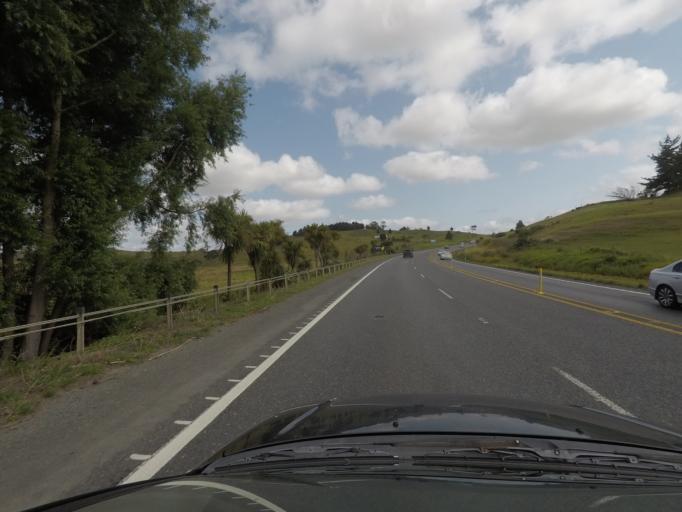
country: NZ
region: Northland
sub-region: Whangarei
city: Whangarei
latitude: -35.8156
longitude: 174.2971
